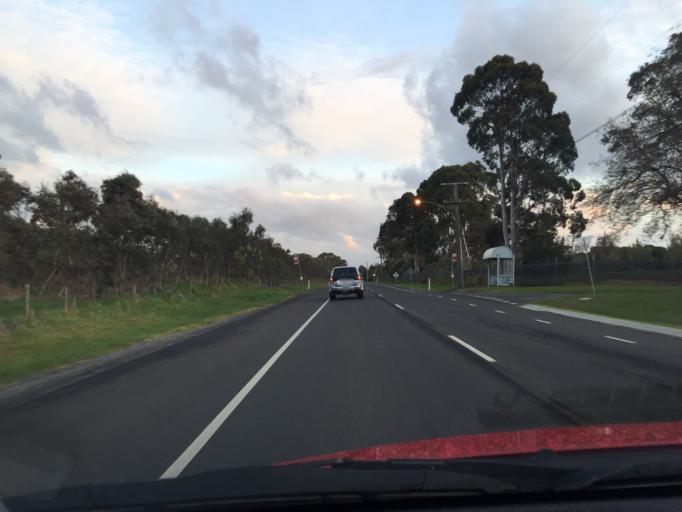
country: AU
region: Victoria
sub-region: Frankston
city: Sandhurst
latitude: -38.0640
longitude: 145.1823
